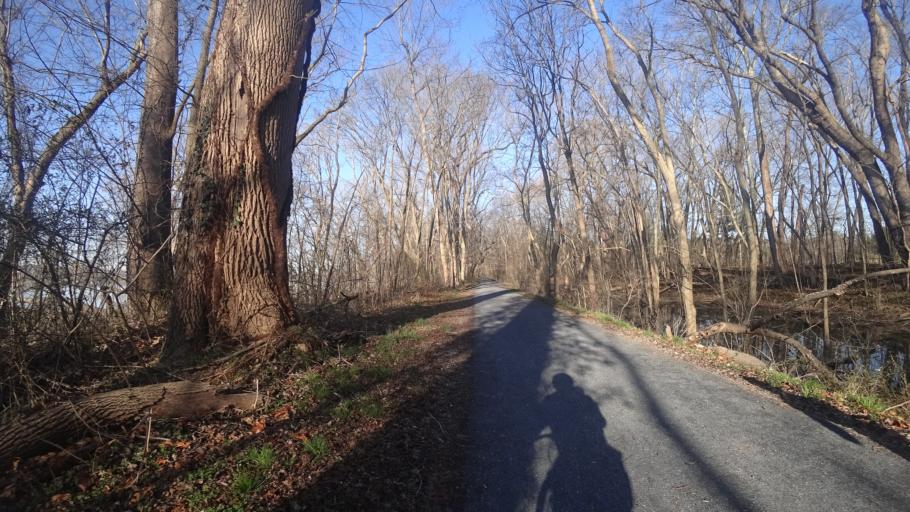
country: US
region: Virginia
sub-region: Loudoun County
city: Lowes Island
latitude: 39.0685
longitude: -77.3362
